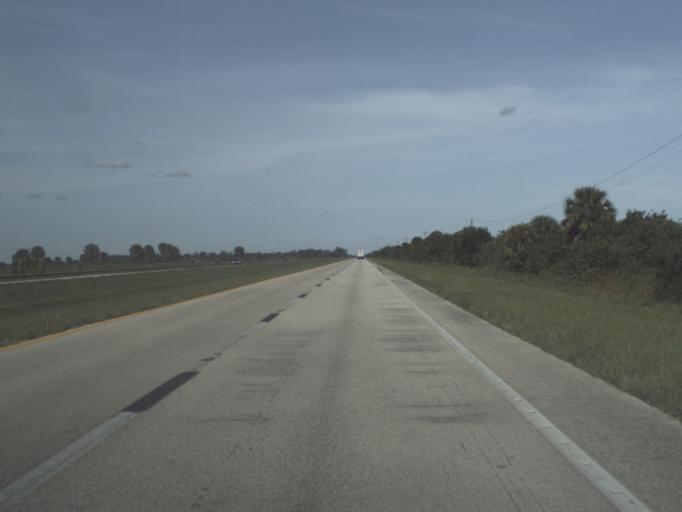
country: US
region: Florida
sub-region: Glades County
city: Moore Haven
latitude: 26.8407
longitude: -81.1958
